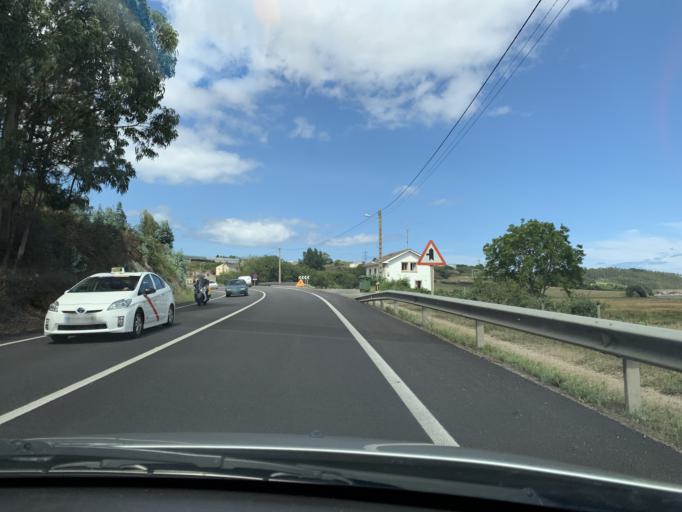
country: ES
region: Galicia
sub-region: Provincia de Lugo
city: Foz
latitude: 43.5435
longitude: -7.2698
